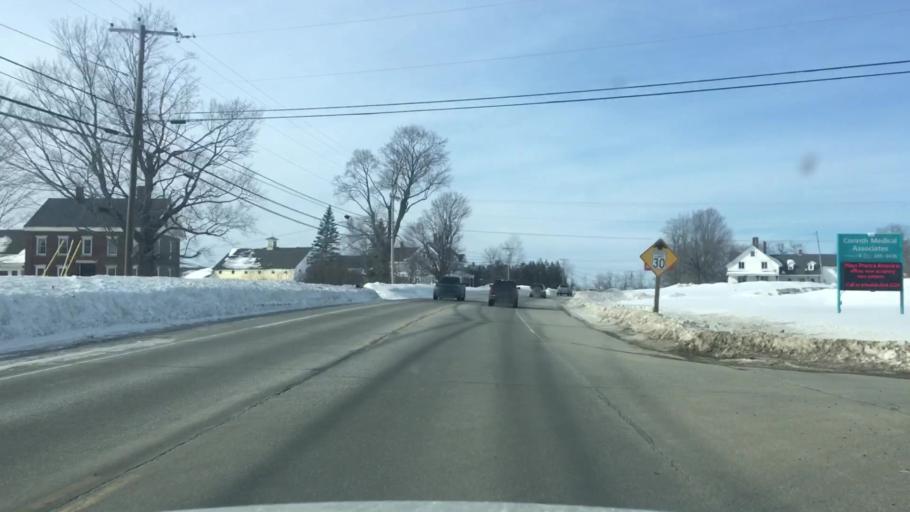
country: US
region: Maine
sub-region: Penobscot County
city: Charleston
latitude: 44.9916
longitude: -69.0172
